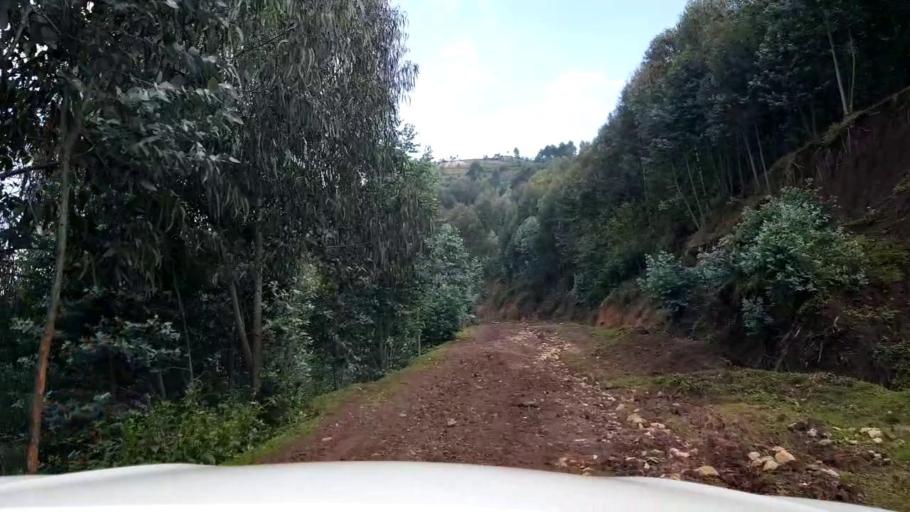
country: RW
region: Western Province
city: Gisenyi
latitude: -1.7205
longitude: 29.3909
